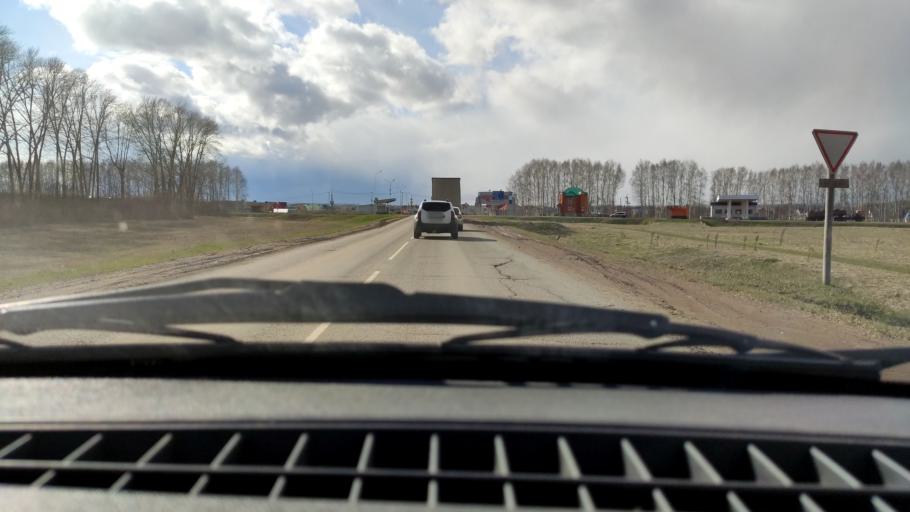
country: RU
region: Bashkortostan
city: Chekmagush
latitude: 55.1295
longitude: 54.6879
